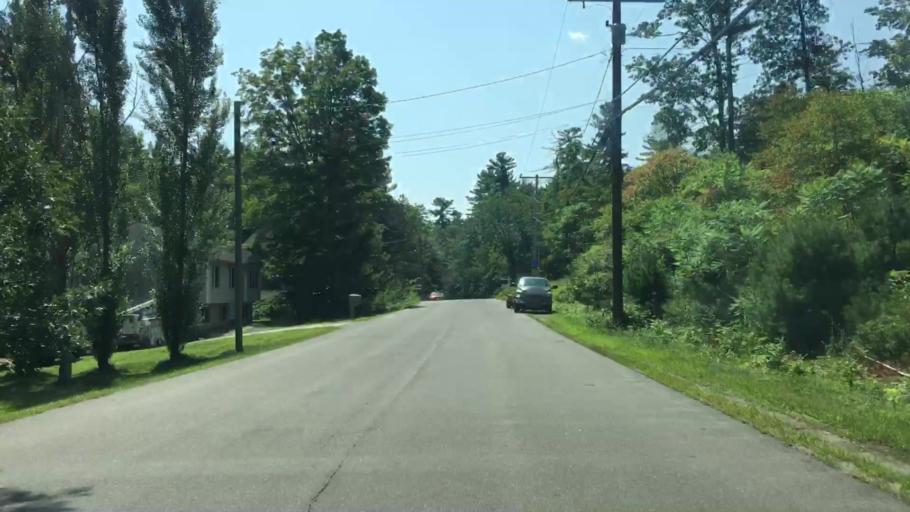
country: US
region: New Hampshire
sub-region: Rockingham County
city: Hampstead
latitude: 42.8741
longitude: -71.2203
